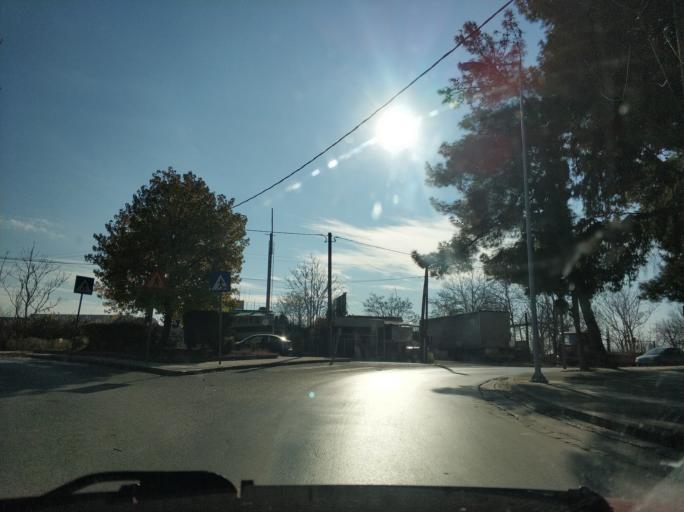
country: GR
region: Central Macedonia
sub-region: Nomos Thessalonikis
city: Pylaia
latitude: 40.5958
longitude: 22.9704
